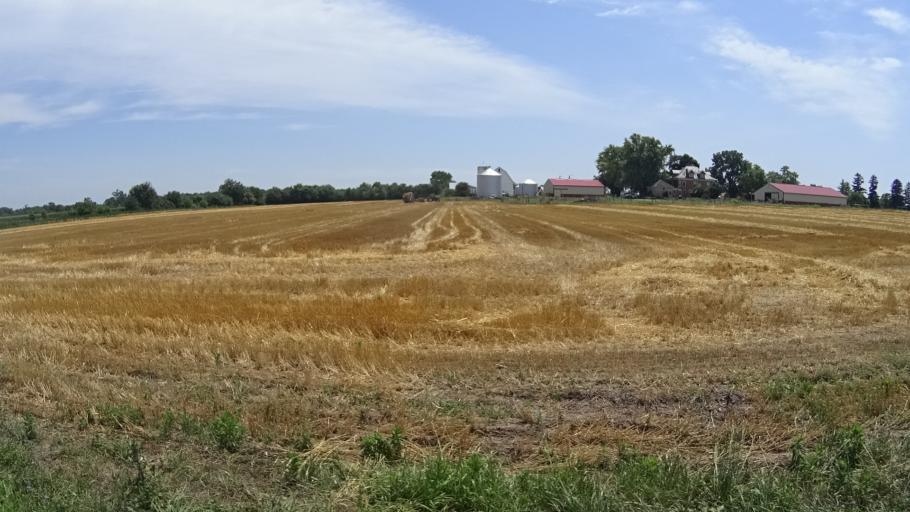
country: US
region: Ohio
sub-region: Erie County
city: Sandusky
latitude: 41.3799
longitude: -82.7845
